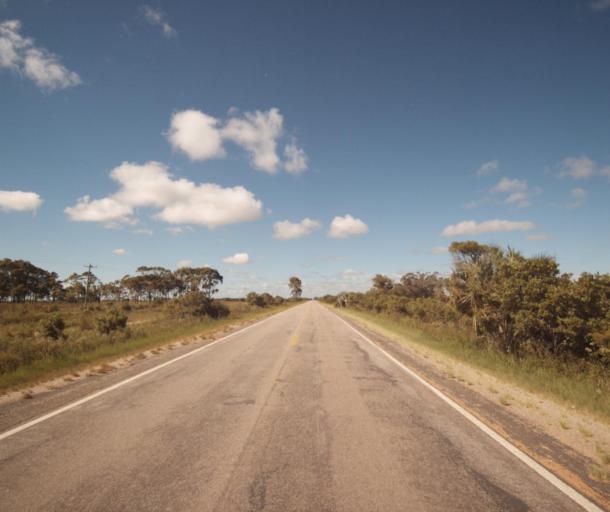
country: BR
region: Rio Grande do Sul
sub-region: Santa Vitoria Do Palmar
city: Santa Vitoria do Palmar
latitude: -33.3825
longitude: -53.1996
